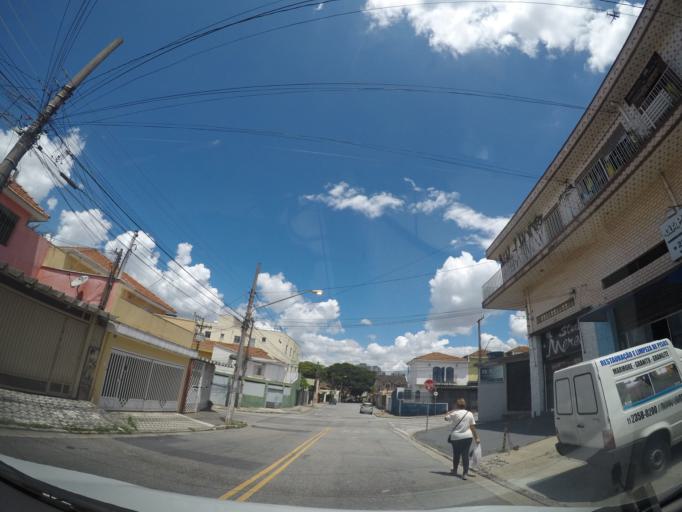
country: BR
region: Sao Paulo
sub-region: Guarulhos
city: Guarulhos
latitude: -23.4484
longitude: -46.5388
